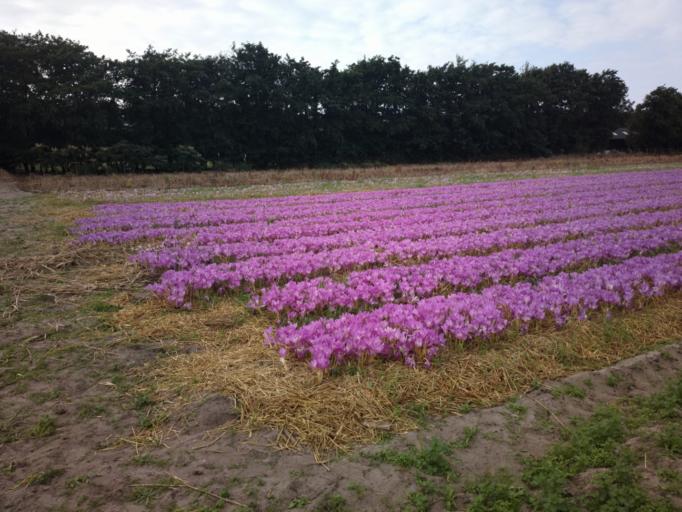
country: NL
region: North Holland
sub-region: Gemeente Texel
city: Den Burg
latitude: 53.0813
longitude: 4.7664
